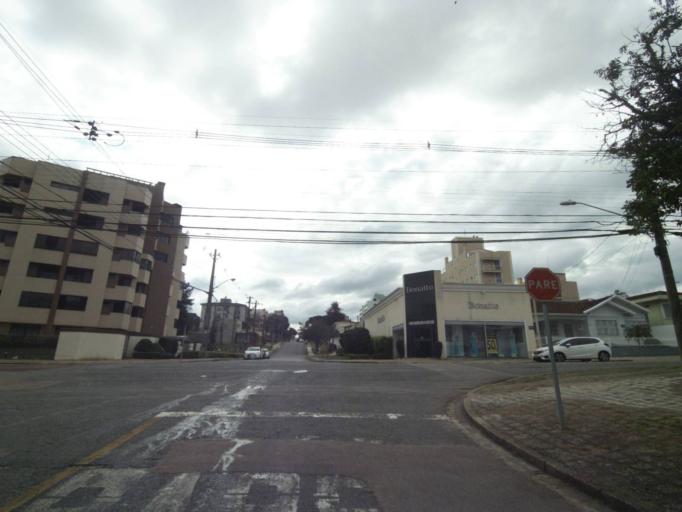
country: BR
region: Parana
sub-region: Curitiba
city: Curitiba
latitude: -25.4054
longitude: -49.2615
